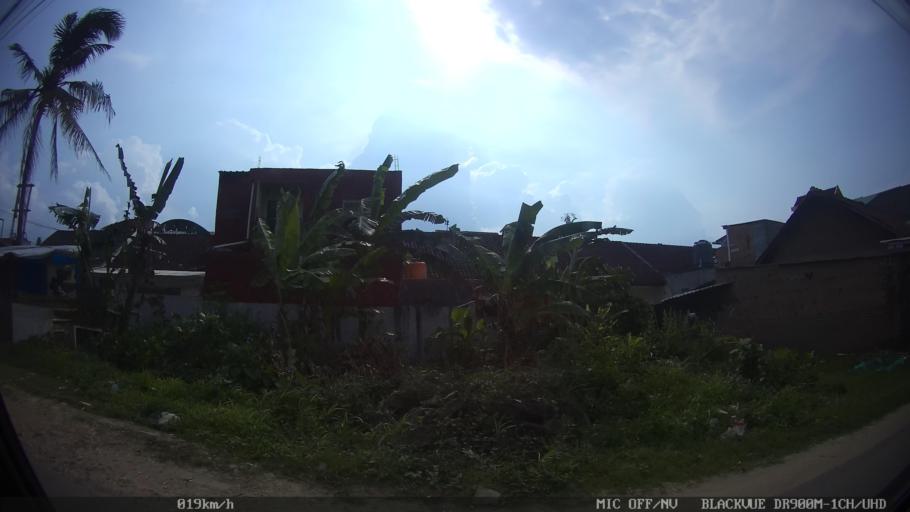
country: ID
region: Lampung
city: Kedaton
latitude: -5.3704
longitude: 105.2206
